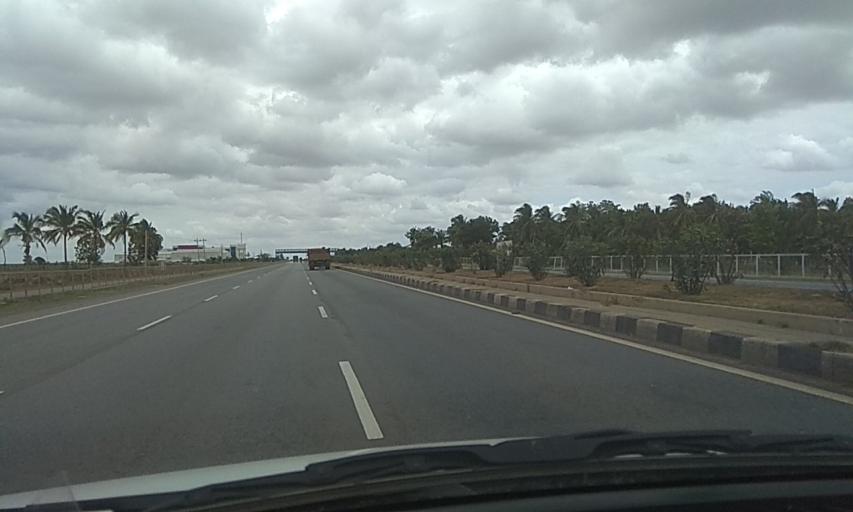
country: IN
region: Karnataka
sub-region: Chitradurga
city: Hiriyur
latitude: 13.8738
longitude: 76.6998
